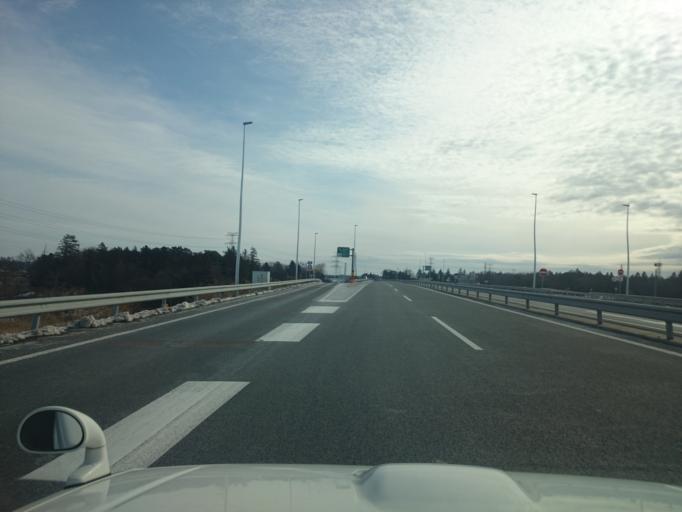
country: JP
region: Ibaraki
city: Sakai
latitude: 36.1256
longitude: 139.8050
